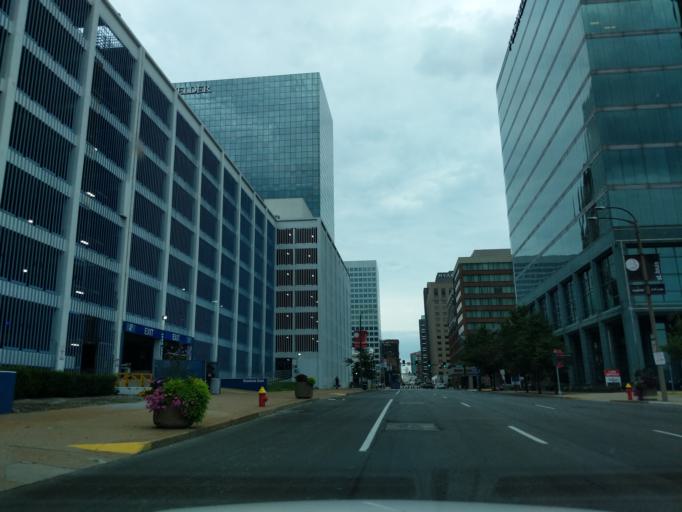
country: US
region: Missouri
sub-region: City of Saint Louis
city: St. Louis
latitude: 38.6232
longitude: -90.1897
